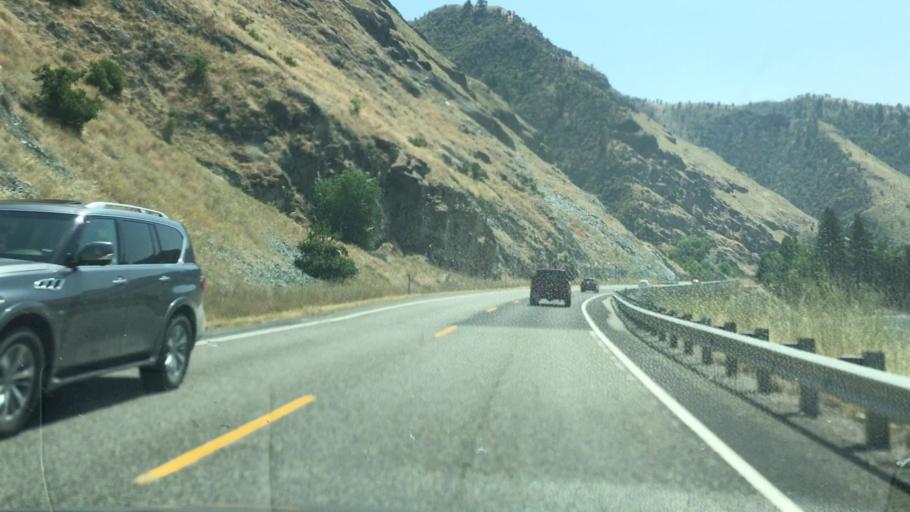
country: US
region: Idaho
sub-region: Idaho County
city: Grangeville
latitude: 45.6072
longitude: -116.2721
